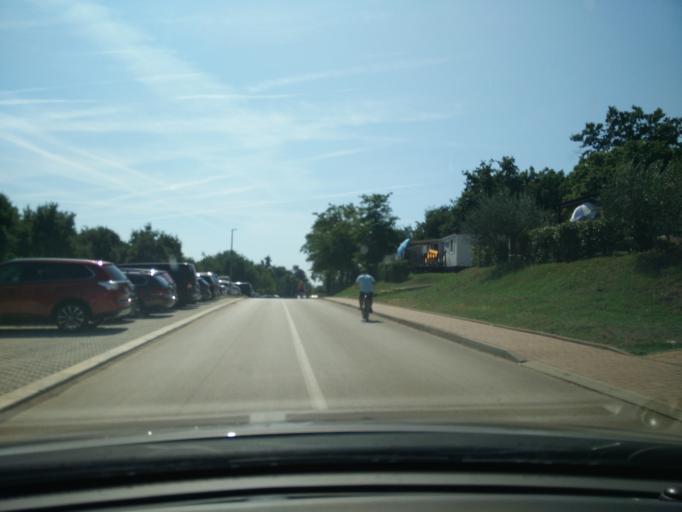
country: HR
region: Istarska
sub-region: Grad Porec
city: Porec
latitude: 45.1901
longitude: 13.5961
